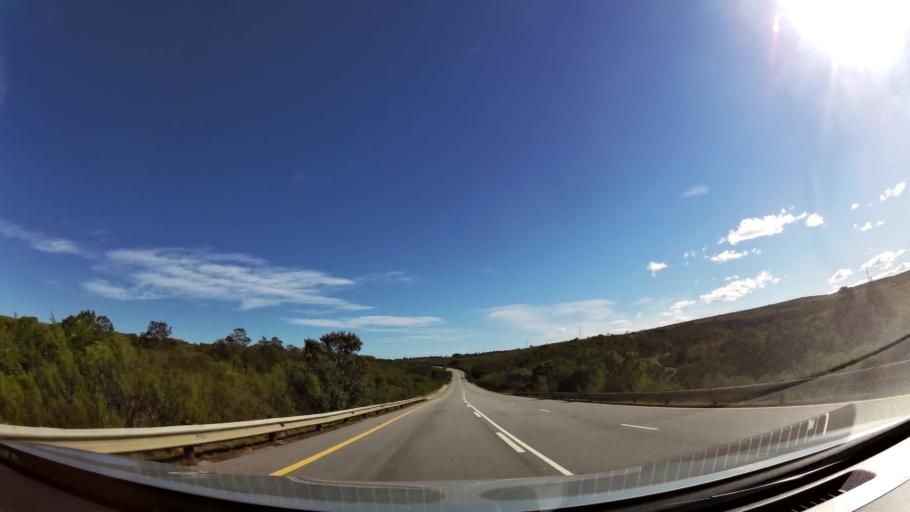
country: ZA
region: Eastern Cape
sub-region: Cacadu District Municipality
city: Kruisfontein
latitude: -34.0138
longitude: 24.6394
